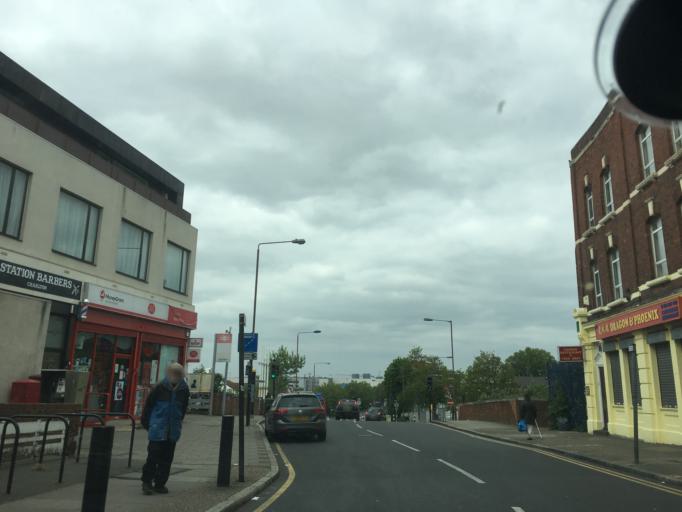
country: GB
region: England
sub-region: Greater London
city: Blackheath
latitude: 51.4866
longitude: 0.0321
